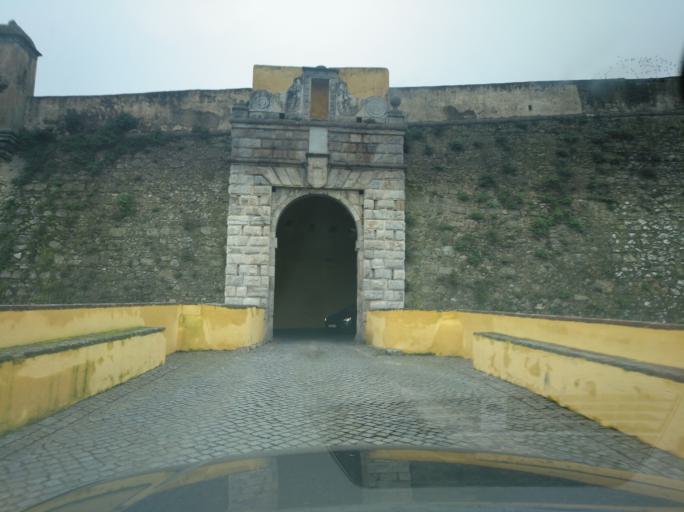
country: PT
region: Portalegre
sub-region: Elvas
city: Elvas
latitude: 38.8826
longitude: -7.1599
